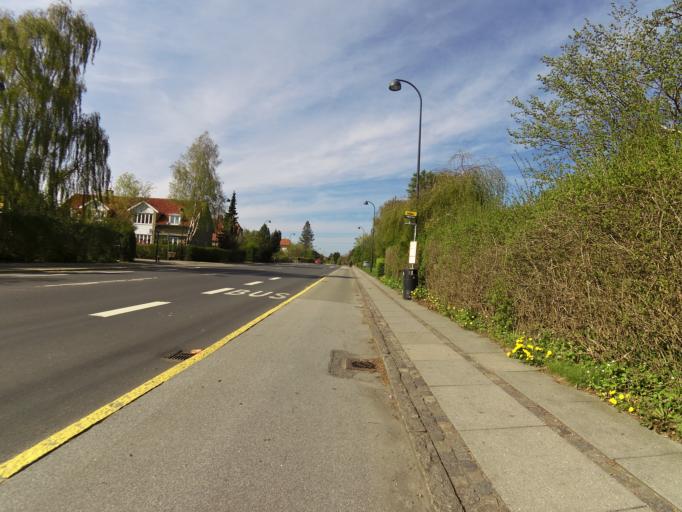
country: DK
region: Capital Region
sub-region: Lyngby-Tarbaek Kommune
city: Kongens Lyngby
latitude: 55.7432
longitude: 12.5234
